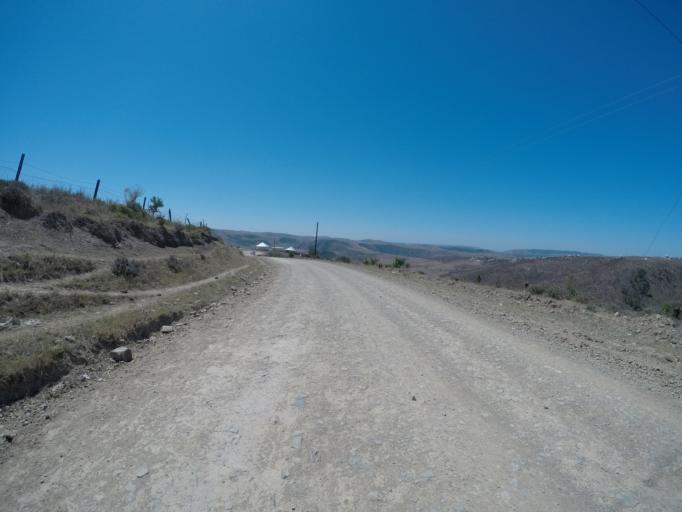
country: ZA
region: Eastern Cape
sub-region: OR Tambo District Municipality
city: Mthatha
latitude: -31.8796
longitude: 28.8761
